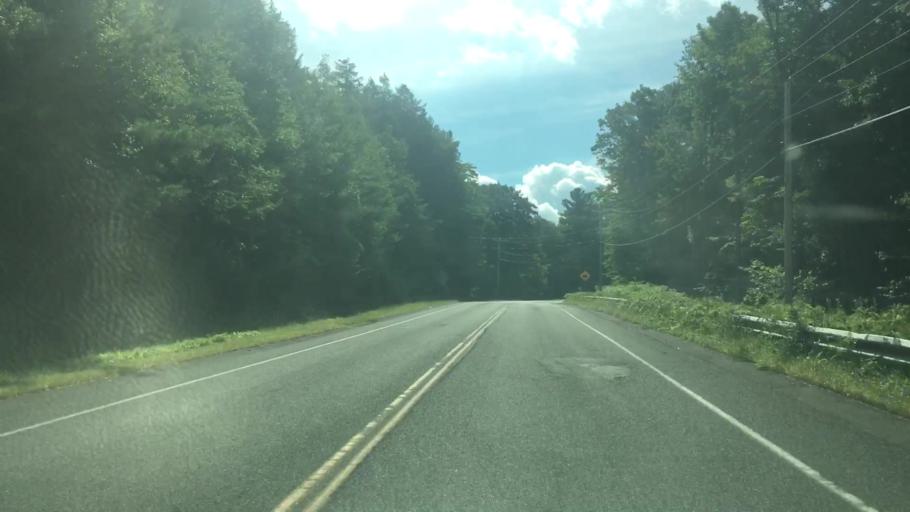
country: US
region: Massachusetts
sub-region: Franklin County
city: Colrain
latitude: 42.6685
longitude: -72.6847
